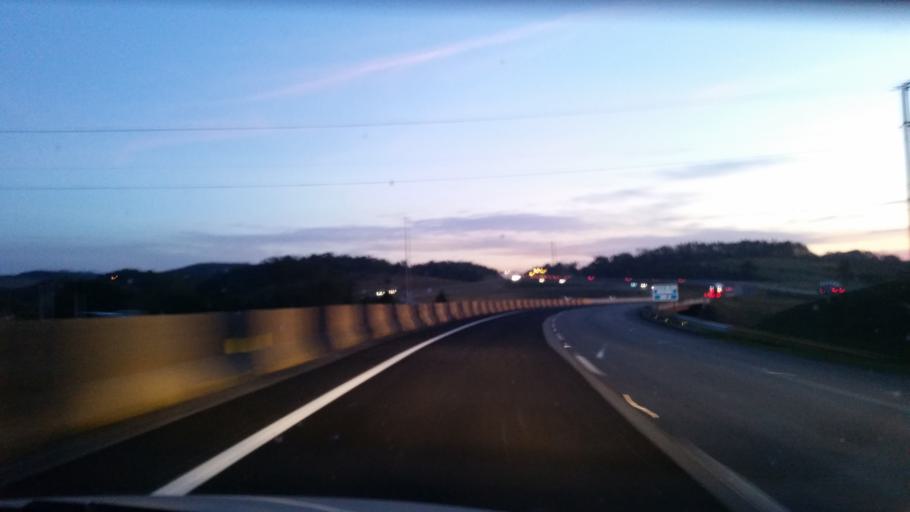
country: BR
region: Sao Paulo
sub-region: Santa Isabel
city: Santa Isabel
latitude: -23.3630
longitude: -46.1271
